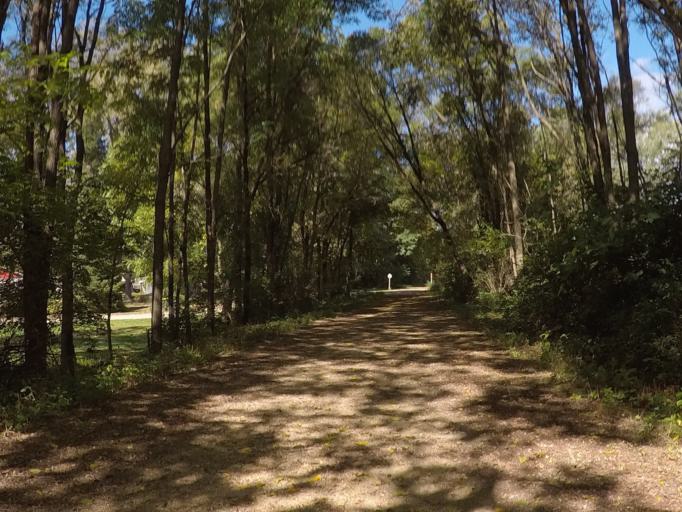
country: US
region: Wisconsin
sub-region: Richland County
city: Richland Center
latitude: 43.2195
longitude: -90.2937
